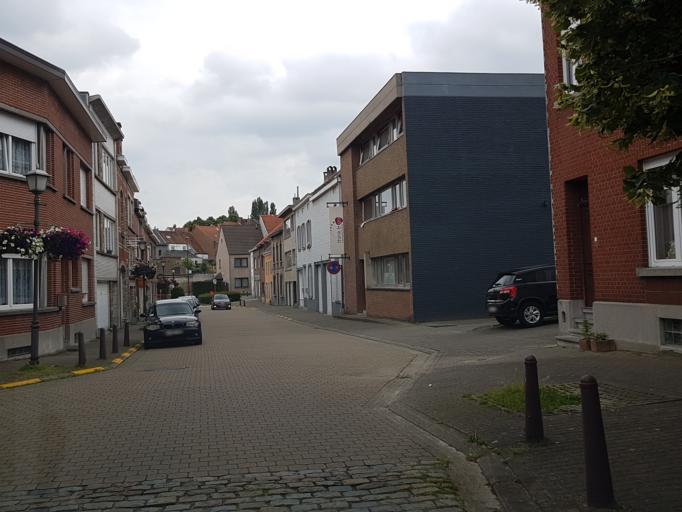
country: BE
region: Flanders
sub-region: Provincie Vlaams-Brabant
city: Kraainem
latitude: 50.8689
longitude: 4.4498
